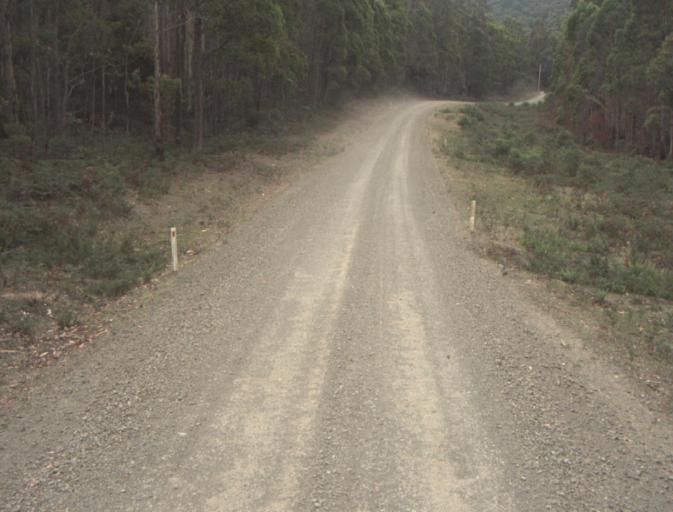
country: AU
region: Tasmania
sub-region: Dorset
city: Scottsdale
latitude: -41.4317
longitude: 147.5146
